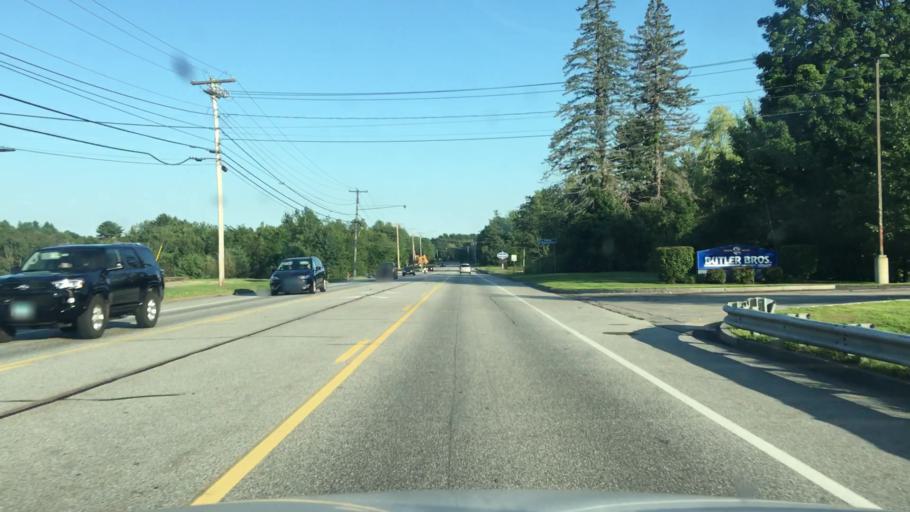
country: US
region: Maine
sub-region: Androscoggin County
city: Lisbon
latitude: 44.0566
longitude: -70.1419
